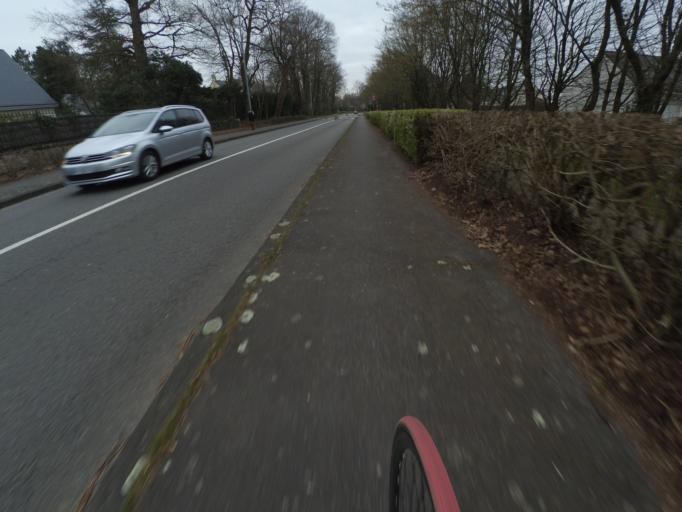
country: FR
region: Pays de la Loire
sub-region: Departement de la Loire-Atlantique
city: Sainte-Luce-sur-Loire
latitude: 47.2754
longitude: -1.4836
